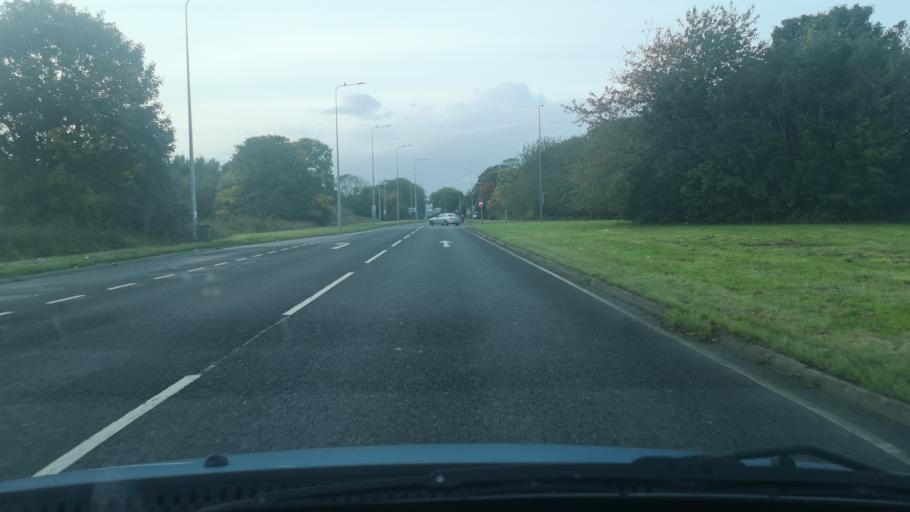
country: GB
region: England
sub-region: North Lincolnshire
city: Crowle
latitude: 53.5850
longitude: -0.8167
